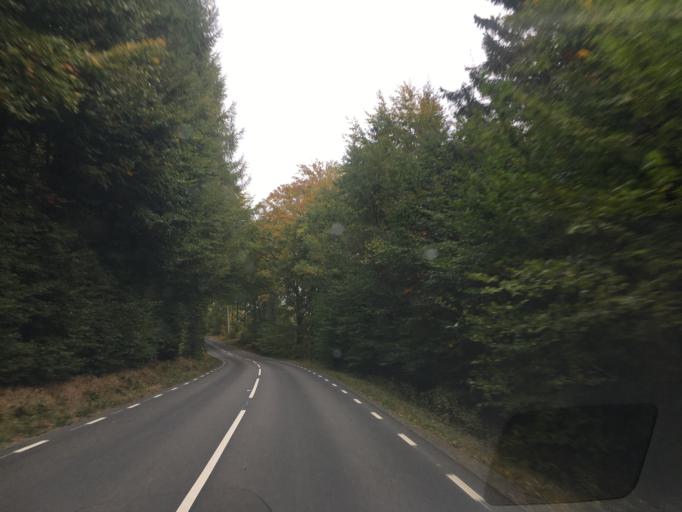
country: SE
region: Skane
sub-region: Simrishamns Kommun
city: Kivik
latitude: 55.6329
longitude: 14.1058
